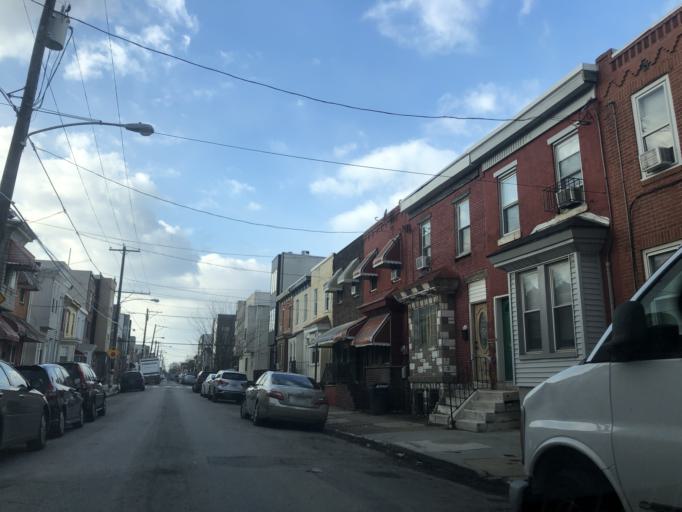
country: US
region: Pennsylvania
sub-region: Philadelphia County
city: Philadelphia
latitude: 39.9338
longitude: -75.1749
